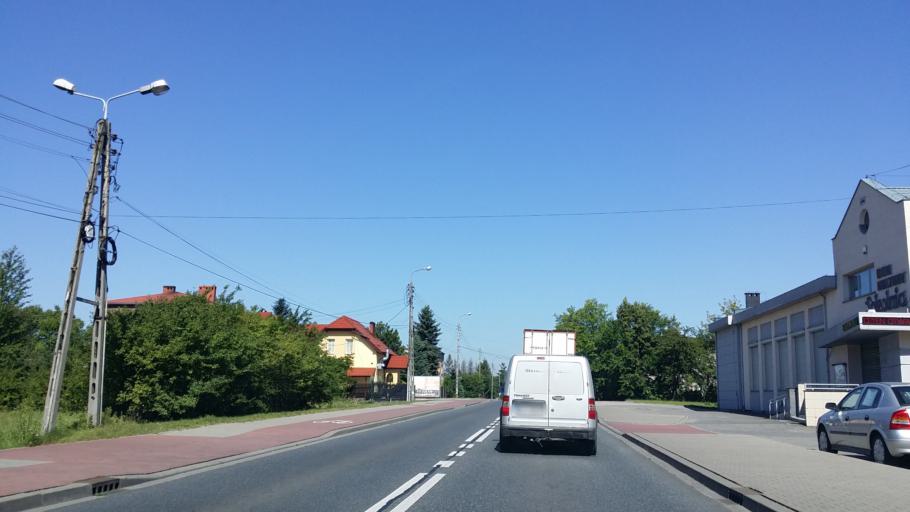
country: PL
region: Silesian Voivodeship
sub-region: Powiat bierunsko-ledzinski
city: Imielin
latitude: 50.1539
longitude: 19.1801
